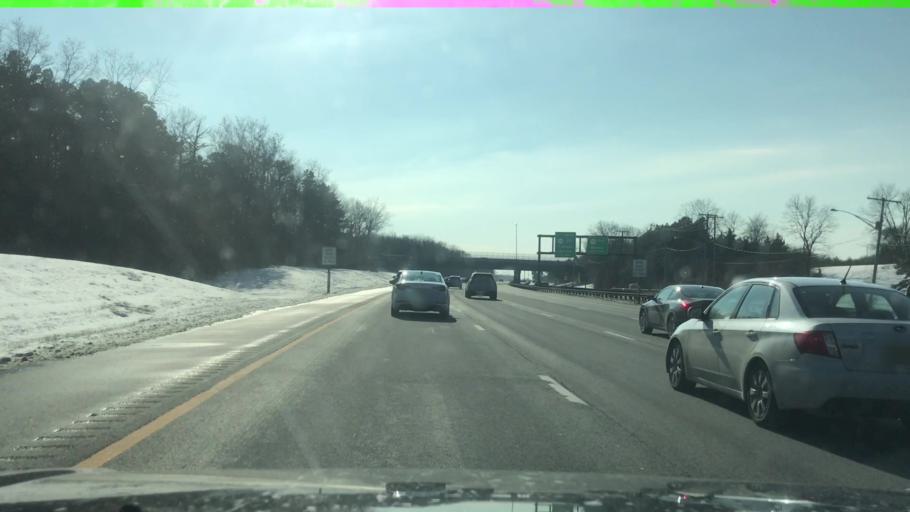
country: US
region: New Jersey
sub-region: Monmouth County
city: Shark River Hills
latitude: 40.1730
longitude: -74.1005
